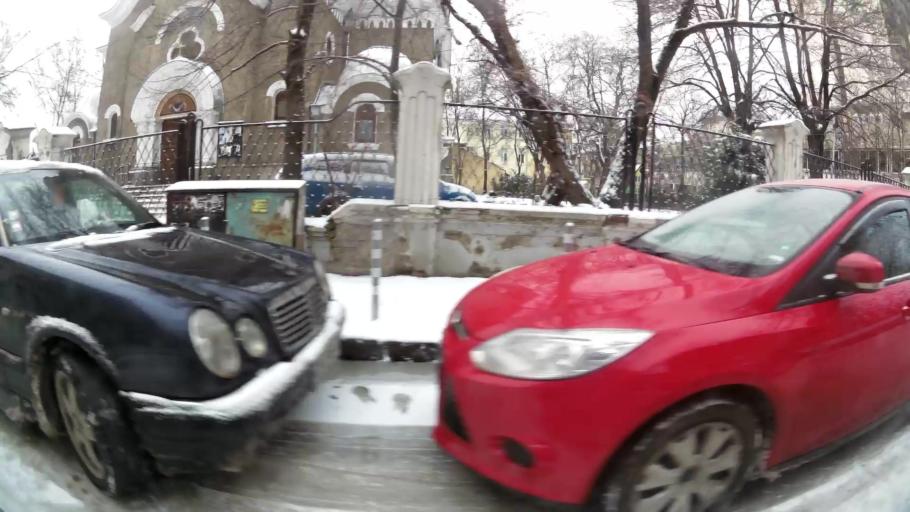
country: BG
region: Sofia-Capital
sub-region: Stolichna Obshtina
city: Sofia
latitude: 42.6925
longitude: 23.3076
